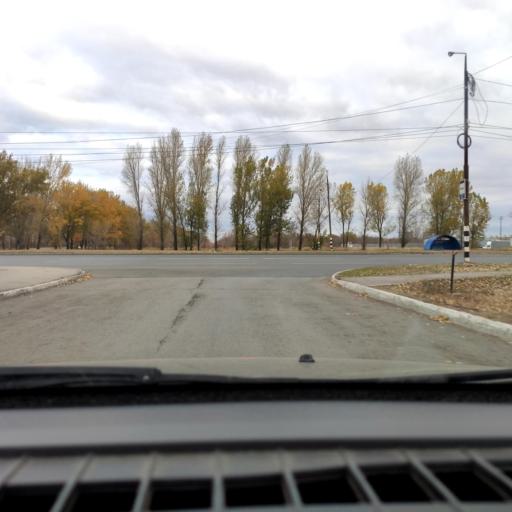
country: RU
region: Samara
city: Podstepki
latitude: 53.5589
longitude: 49.2161
